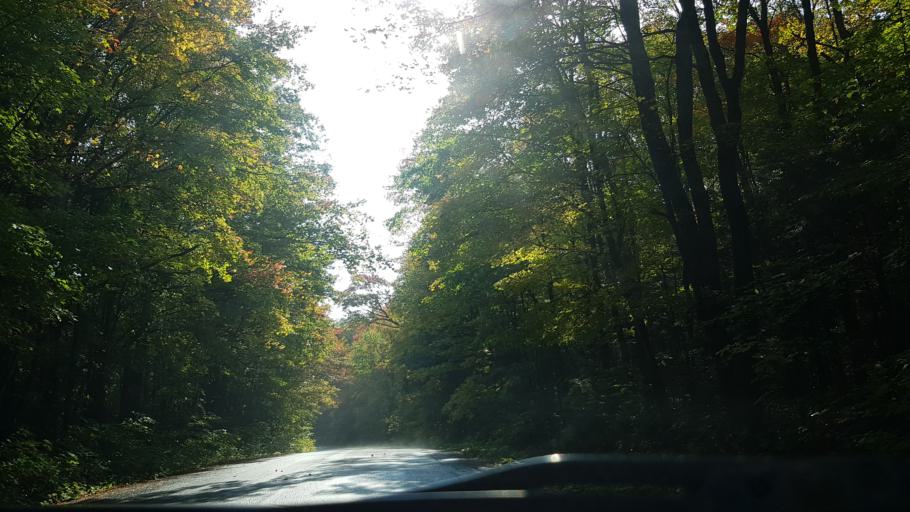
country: CA
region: Ontario
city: Bracebridge
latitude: 44.9578
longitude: -79.2500
